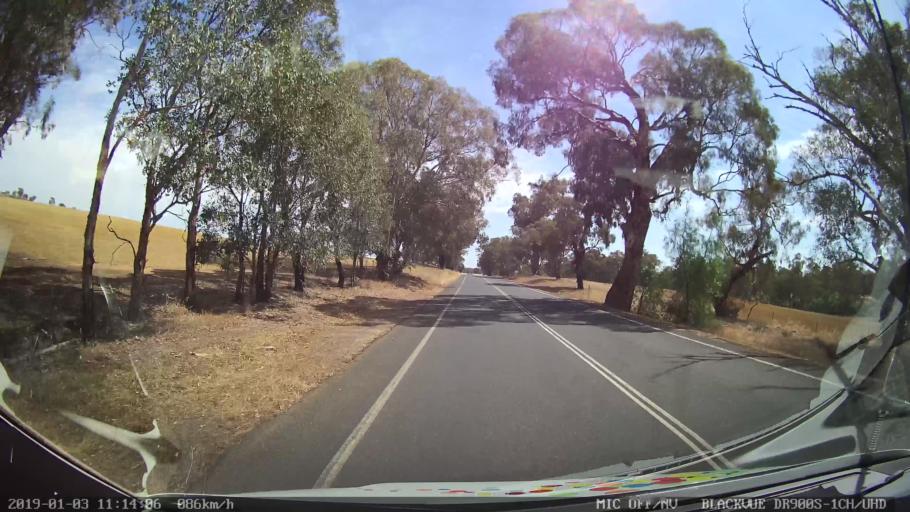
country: AU
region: New South Wales
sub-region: Young
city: Young
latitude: -34.1802
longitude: 148.2604
